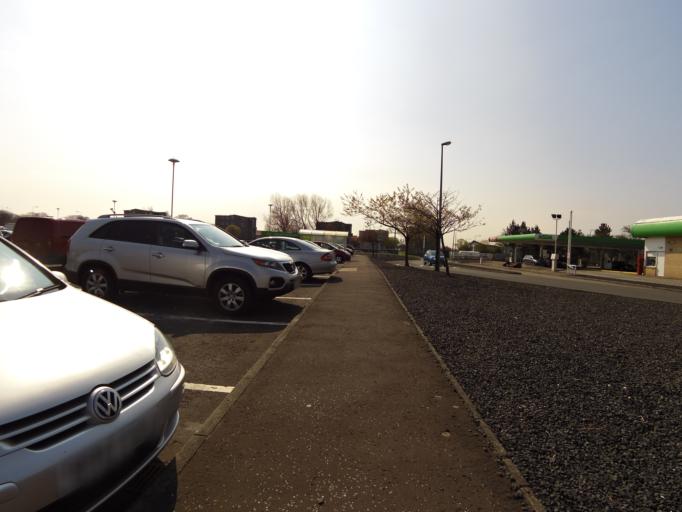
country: GB
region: Scotland
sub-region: Fife
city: Kirkcaldy
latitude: 56.1348
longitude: -3.1470
